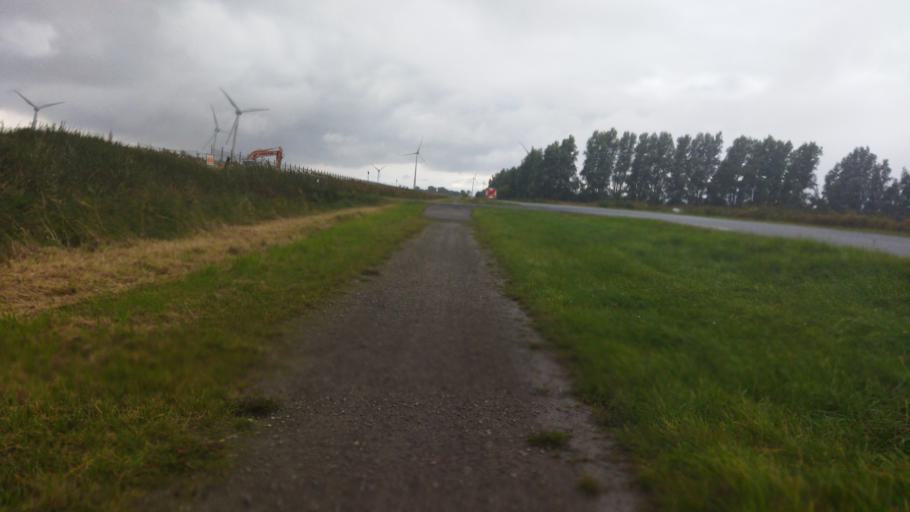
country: DE
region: Lower Saxony
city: Emden
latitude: 53.3529
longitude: 7.1445
